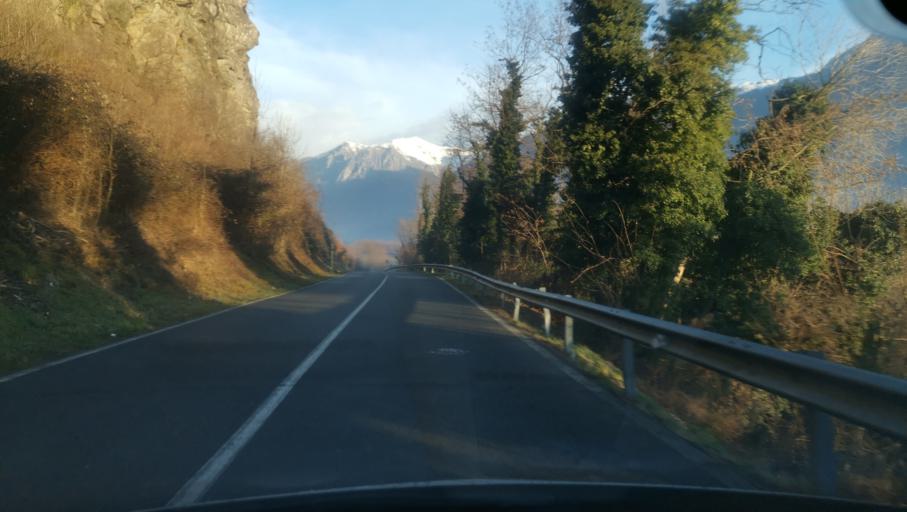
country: IT
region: Piedmont
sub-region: Provincia di Torino
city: Quassolo
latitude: 45.5301
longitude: 7.8330
